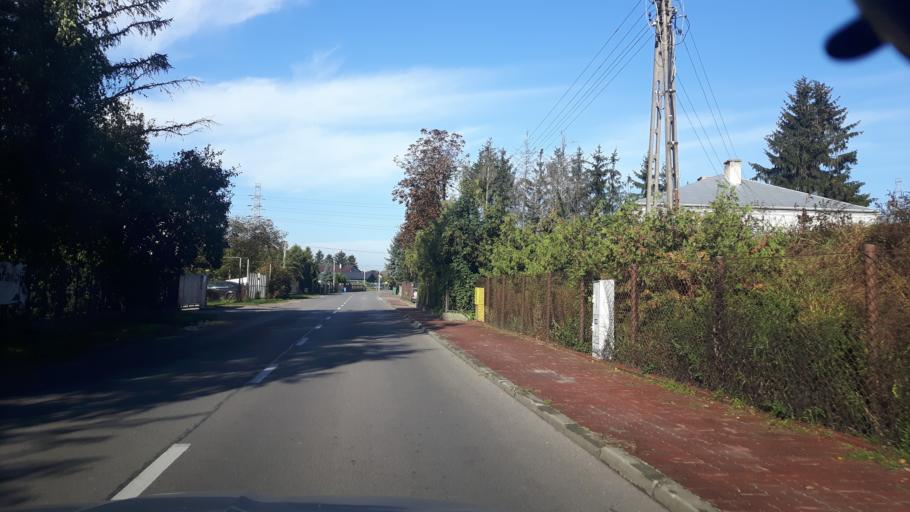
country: PL
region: Masovian Voivodeship
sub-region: Powiat legionowski
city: Michalow-Reginow
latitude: 52.4087
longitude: 20.9721
